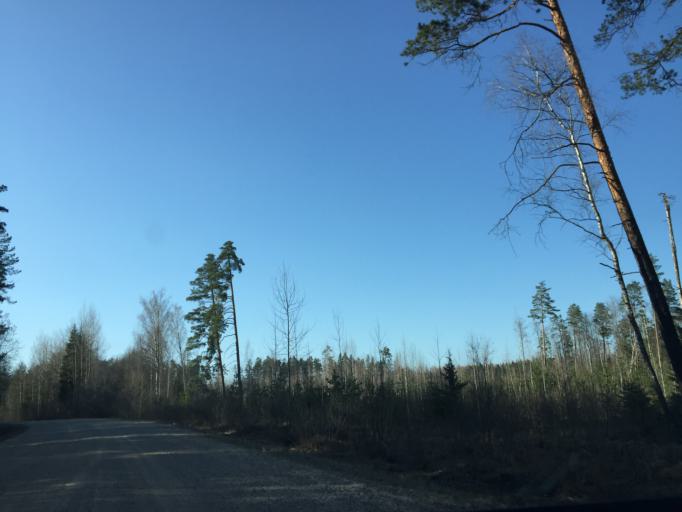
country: LV
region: Ropazu
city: Ropazi
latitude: 56.9550
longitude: 24.7237
